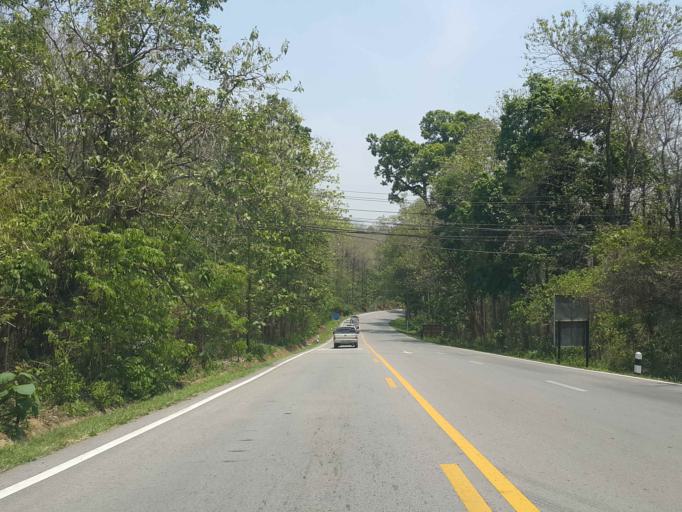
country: TH
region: Chiang Mai
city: Mae On
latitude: 18.9394
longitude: 99.2371
